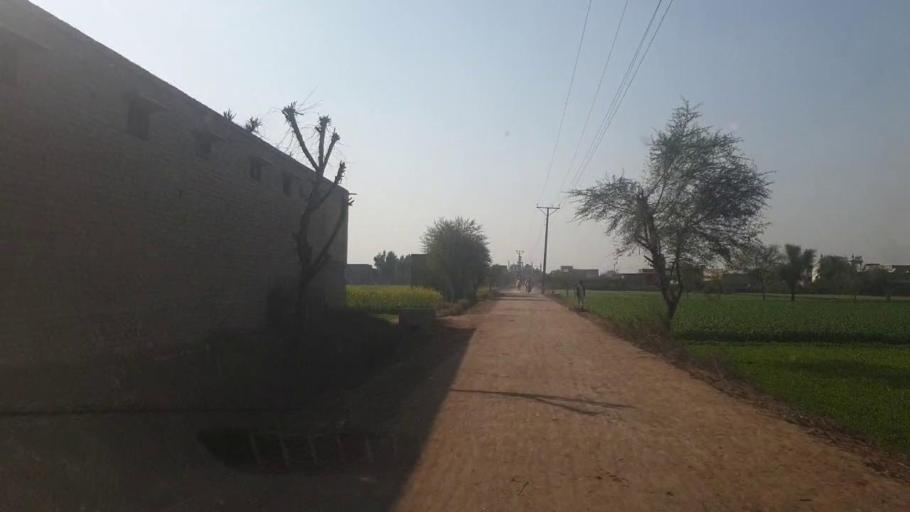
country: PK
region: Sindh
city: Sakrand
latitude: 26.0644
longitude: 68.3813
